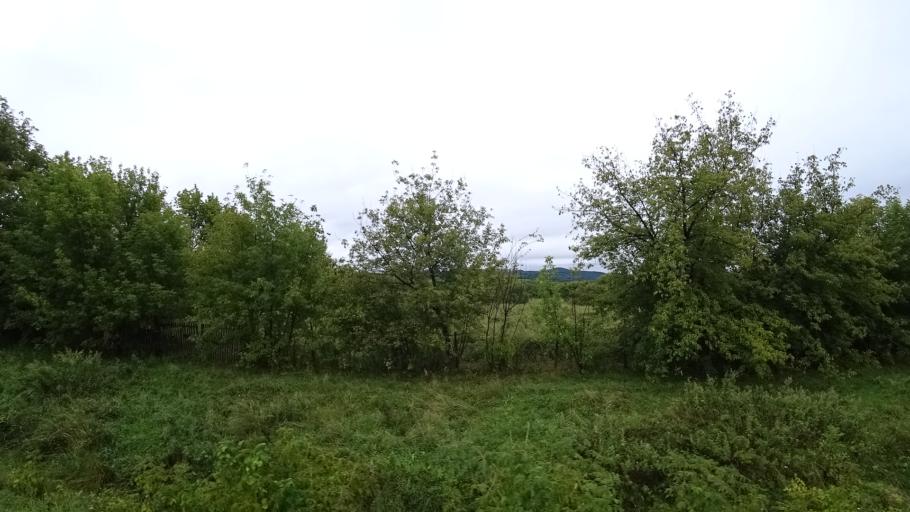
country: RU
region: Primorskiy
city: Monastyrishche
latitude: 44.2686
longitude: 132.4204
